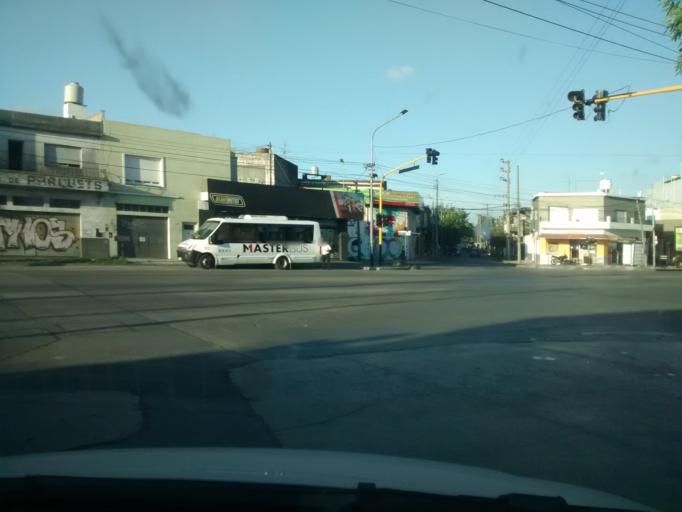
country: AR
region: Buenos Aires
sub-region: Partido de Moron
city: Moron
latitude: -34.6605
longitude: -58.6127
